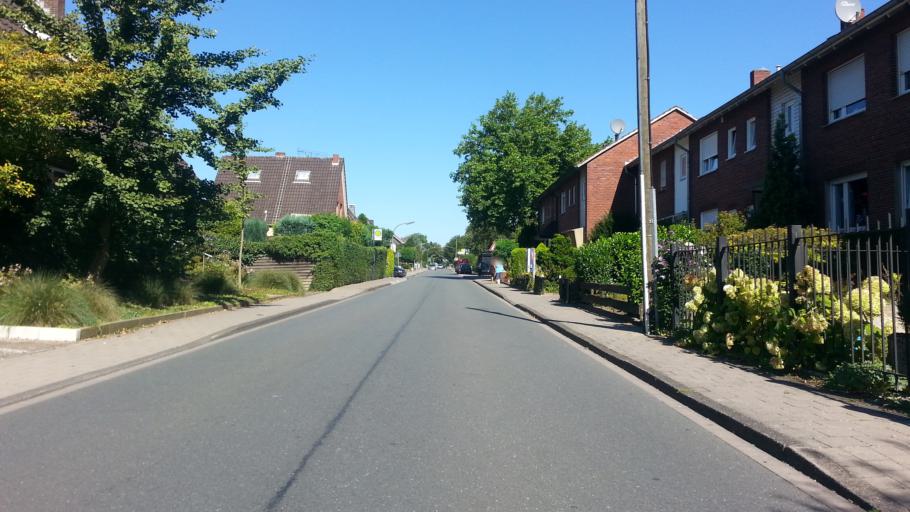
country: DE
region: North Rhine-Westphalia
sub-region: Regierungsbezirk Munster
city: Muenster
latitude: 51.9508
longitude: 7.5374
